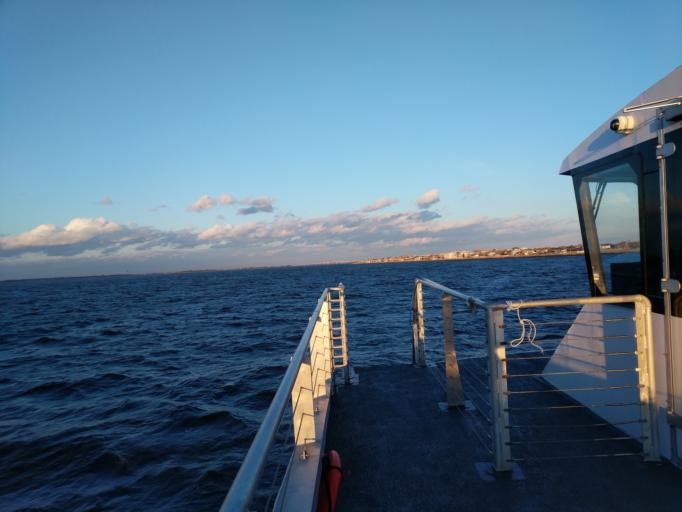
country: US
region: New York
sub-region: Kings County
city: East New York
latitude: 40.5765
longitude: -73.8700
